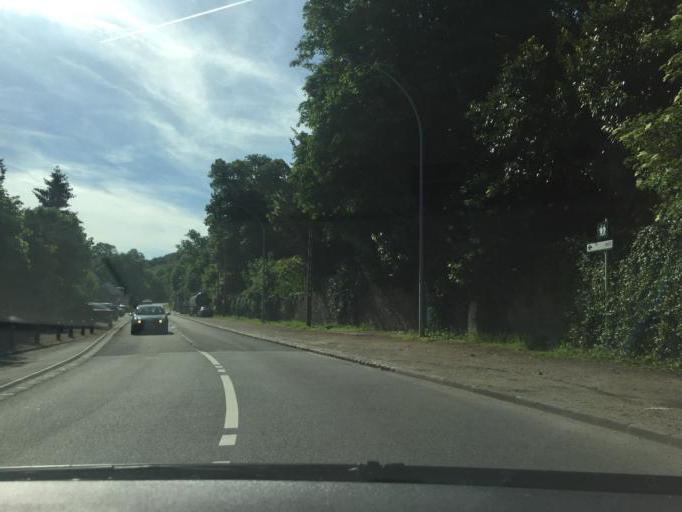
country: FR
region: Ile-de-France
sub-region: Departement des Yvelines
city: Jouy-en-Josas
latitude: 48.7629
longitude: 2.1675
